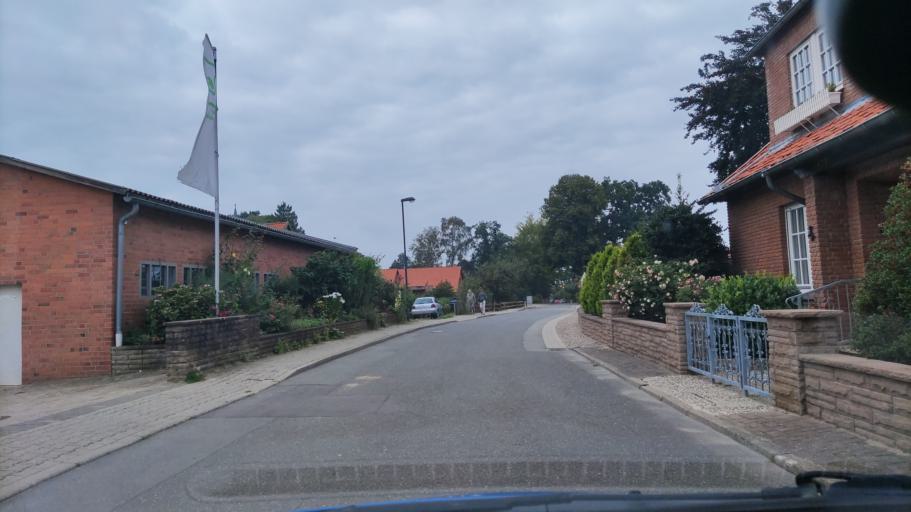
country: DE
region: Lower Saxony
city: Altenmedingen
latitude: 53.1318
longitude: 10.6019
